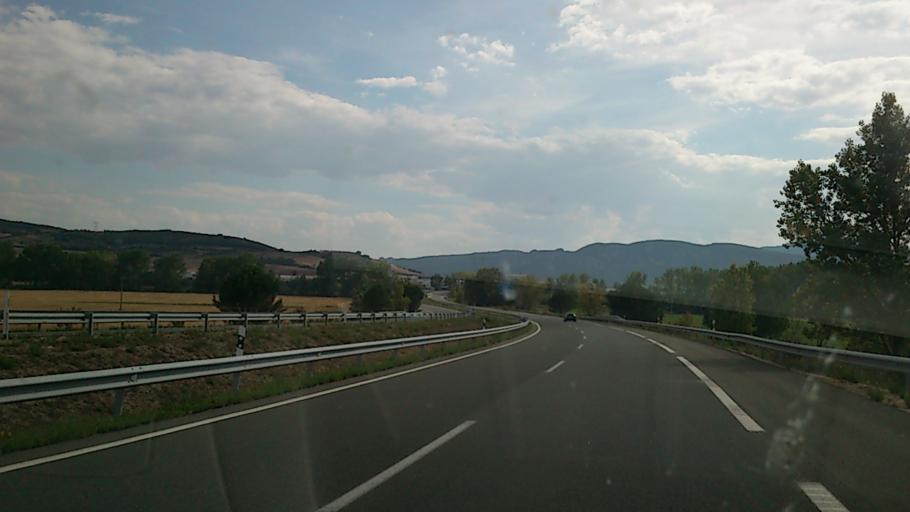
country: ES
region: Basque Country
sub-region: Provincia de Alava
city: Zambrana
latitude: 42.6872
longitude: -2.8919
